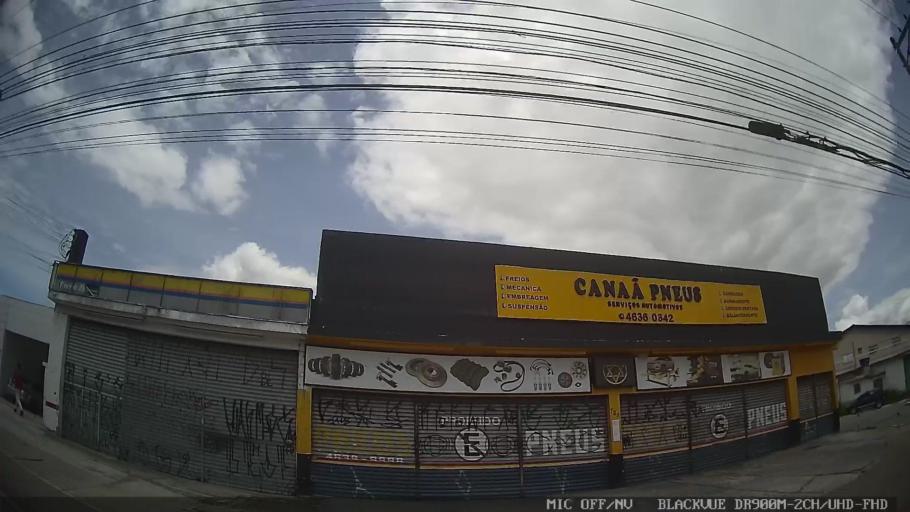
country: BR
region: Sao Paulo
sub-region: Poa
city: Poa
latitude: -23.5347
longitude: -46.3529
